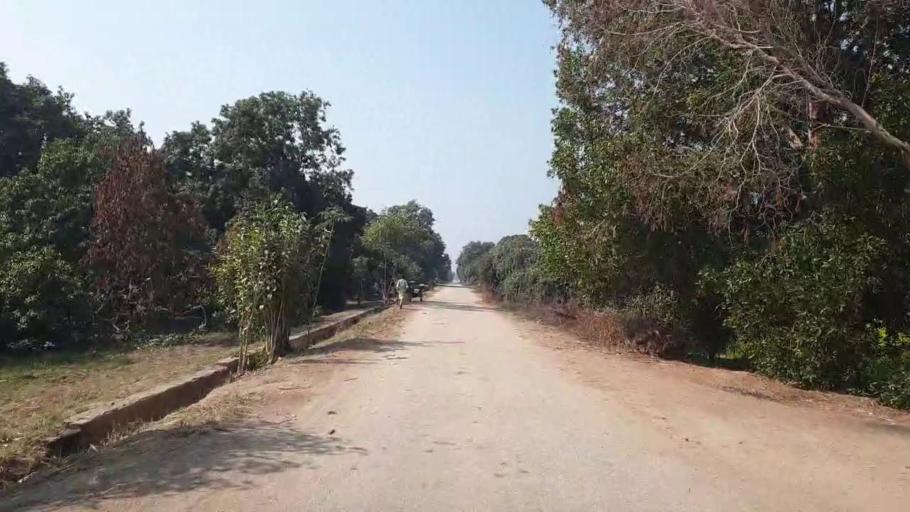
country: PK
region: Sindh
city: Bhit Shah
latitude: 25.7644
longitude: 68.5039
